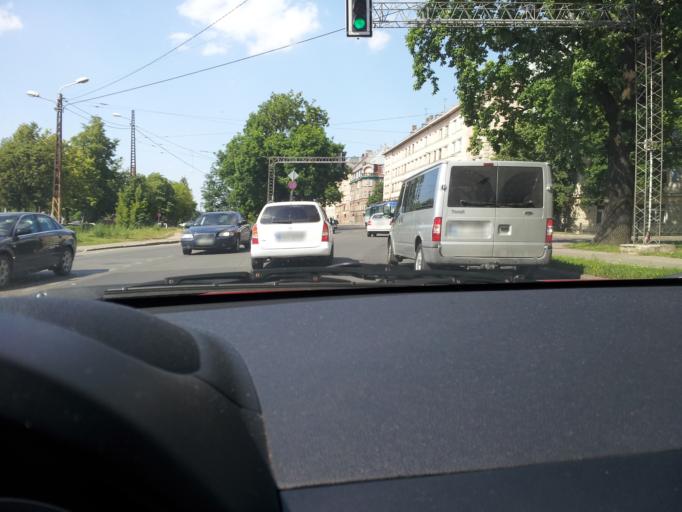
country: LV
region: Riga
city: Riga
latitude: 56.9590
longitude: 24.0983
